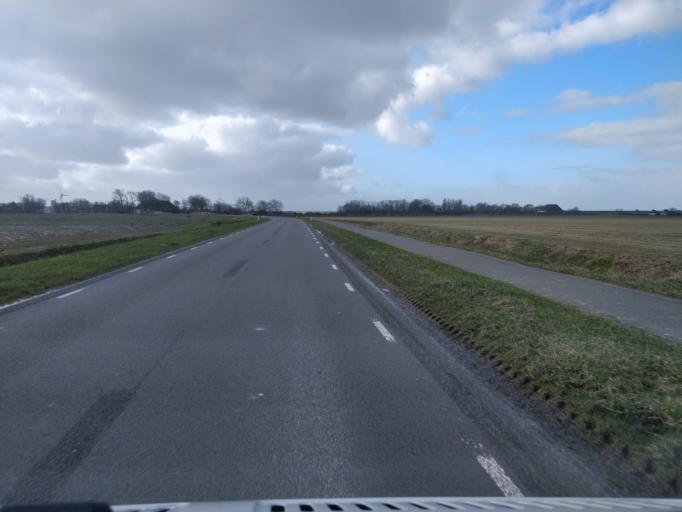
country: NL
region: Friesland
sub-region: Gemeente Franekeradeel
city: Sexbierum
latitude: 53.2059
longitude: 5.4587
